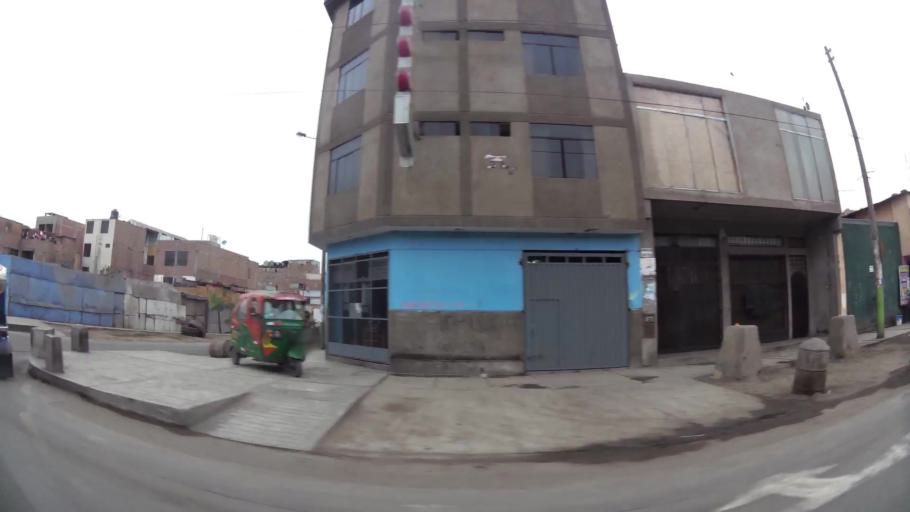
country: PE
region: Lima
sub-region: Lima
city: Vitarte
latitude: -12.0396
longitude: -76.9535
